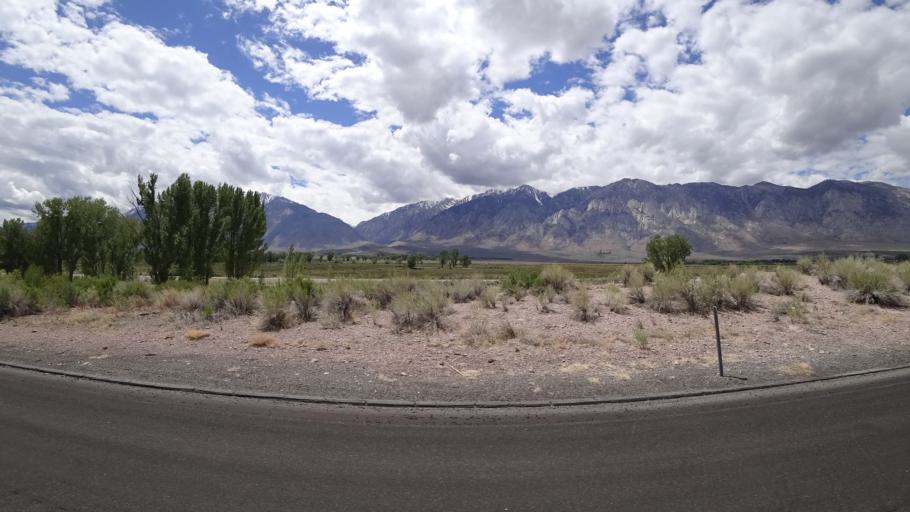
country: US
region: California
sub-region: Inyo County
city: West Bishop
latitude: 37.4411
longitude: -118.5716
